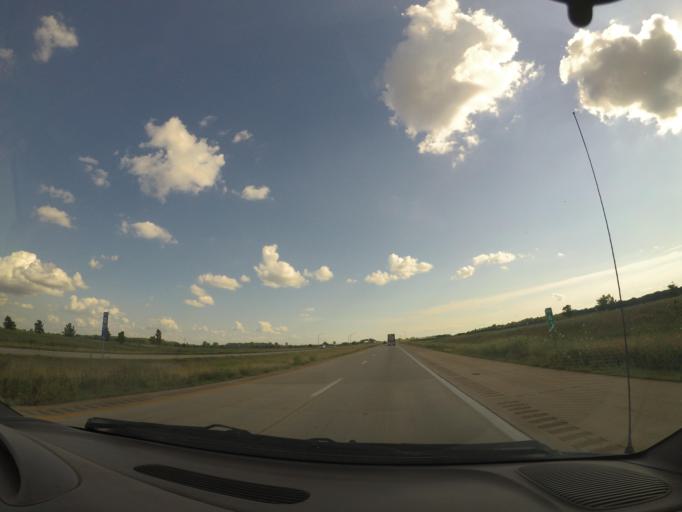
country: US
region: Ohio
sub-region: Lucas County
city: Waterville
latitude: 41.5081
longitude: -83.7547
